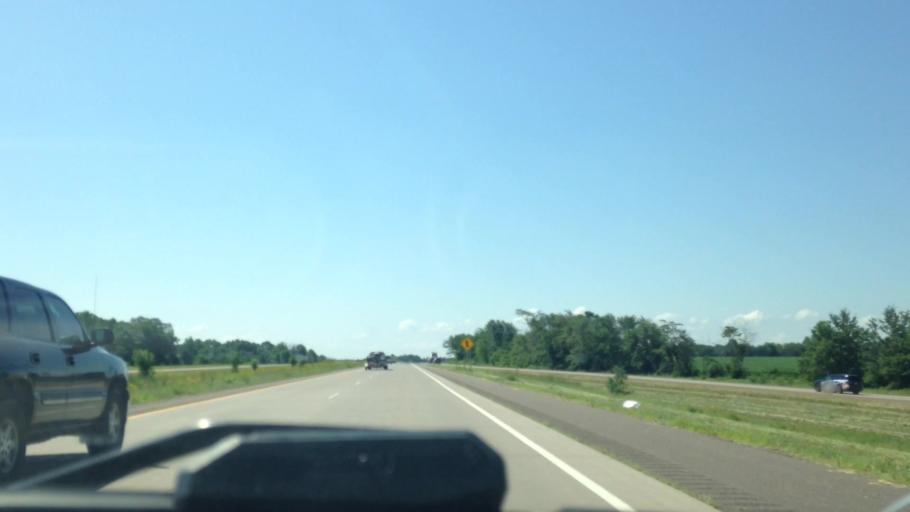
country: US
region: Wisconsin
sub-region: Barron County
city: Rice Lake
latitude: 45.4724
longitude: -91.7589
